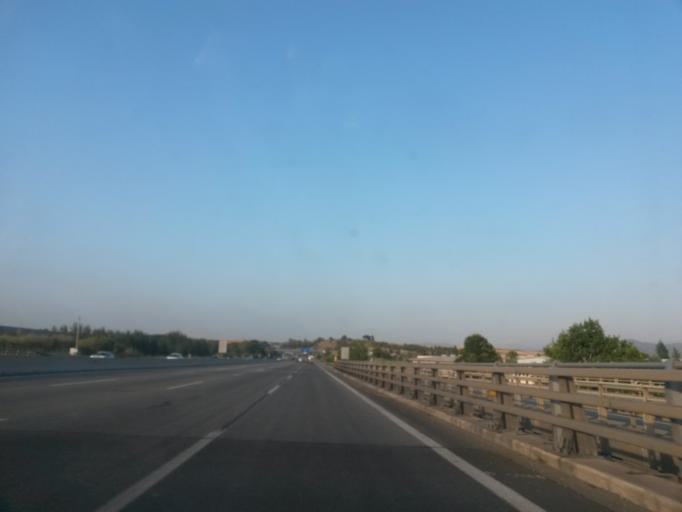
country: ES
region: Catalonia
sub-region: Provincia de Barcelona
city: Santa Perpetua de Mogoda
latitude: 41.5408
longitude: 2.1804
